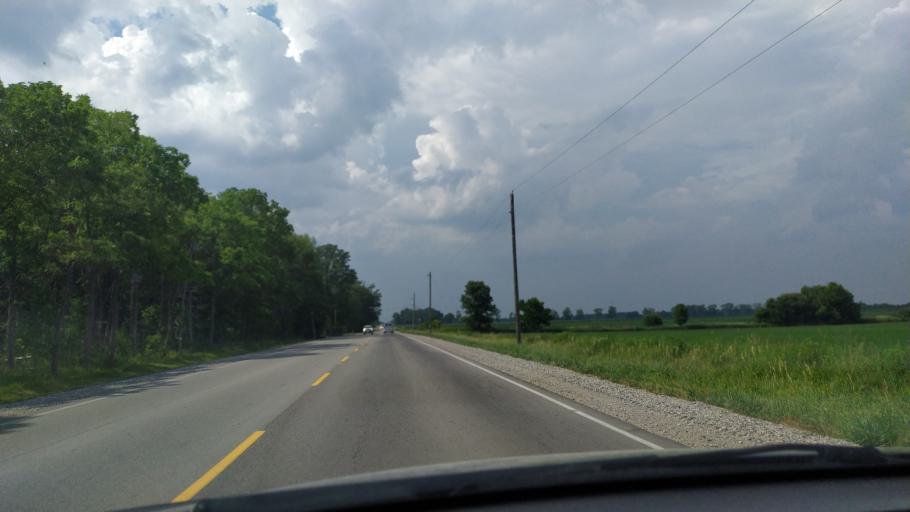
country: CA
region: Ontario
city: Dorchester
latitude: 43.0650
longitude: -81.1380
